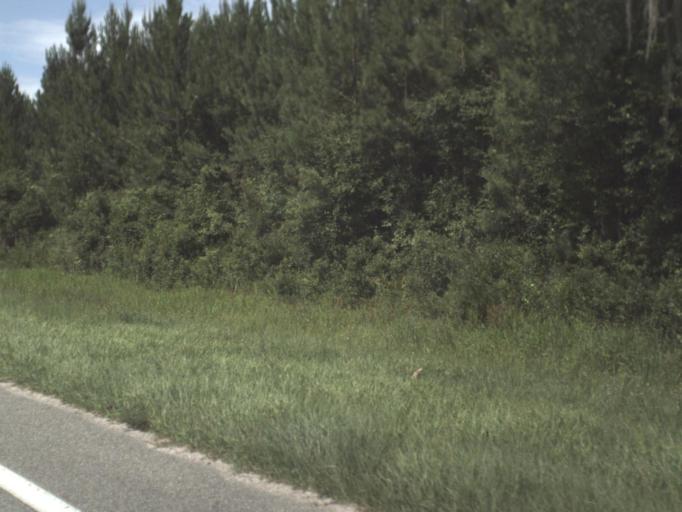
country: US
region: Florida
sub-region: Hamilton County
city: Jasper
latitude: 30.4678
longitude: -82.9309
